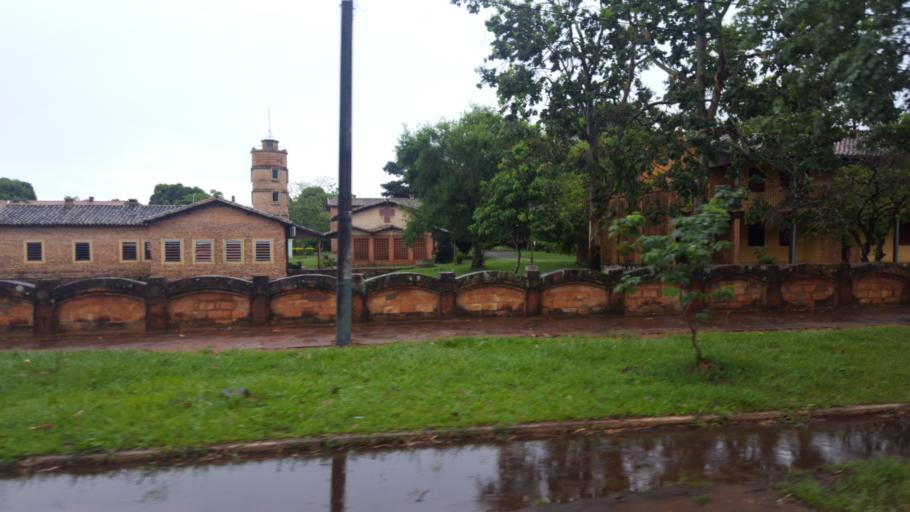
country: PY
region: Misiones
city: San Juan Bautista
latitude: -26.6701
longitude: -57.1470
